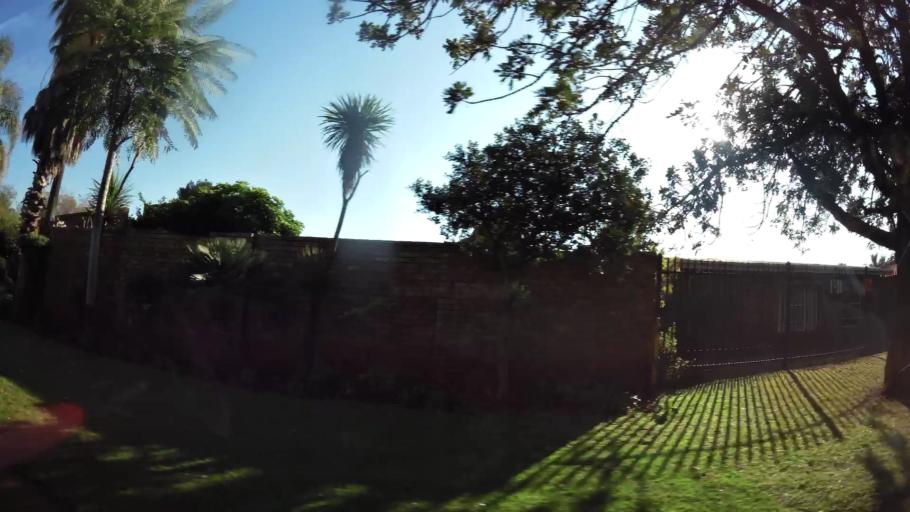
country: ZA
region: Gauteng
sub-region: City of Tshwane Metropolitan Municipality
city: Pretoria
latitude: -25.6716
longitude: 28.2030
